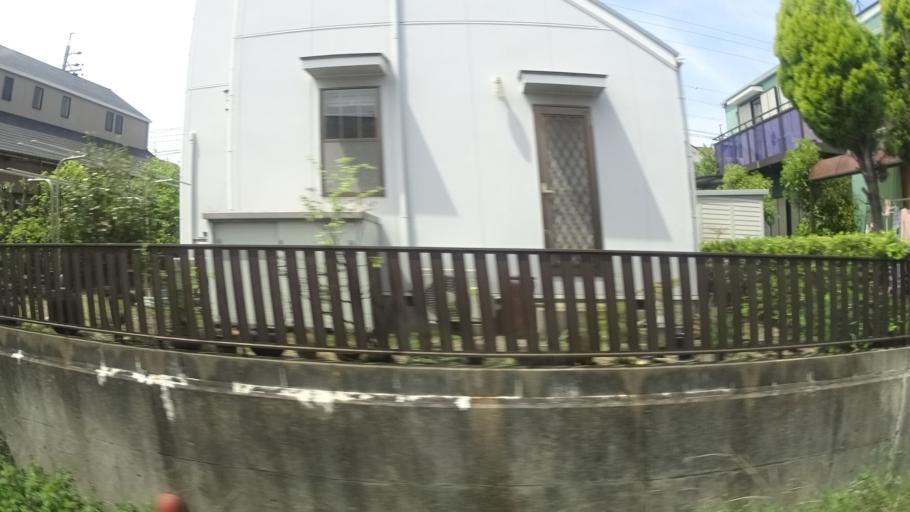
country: JP
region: Mie
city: Tsu-shi
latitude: 34.6925
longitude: 136.5086
